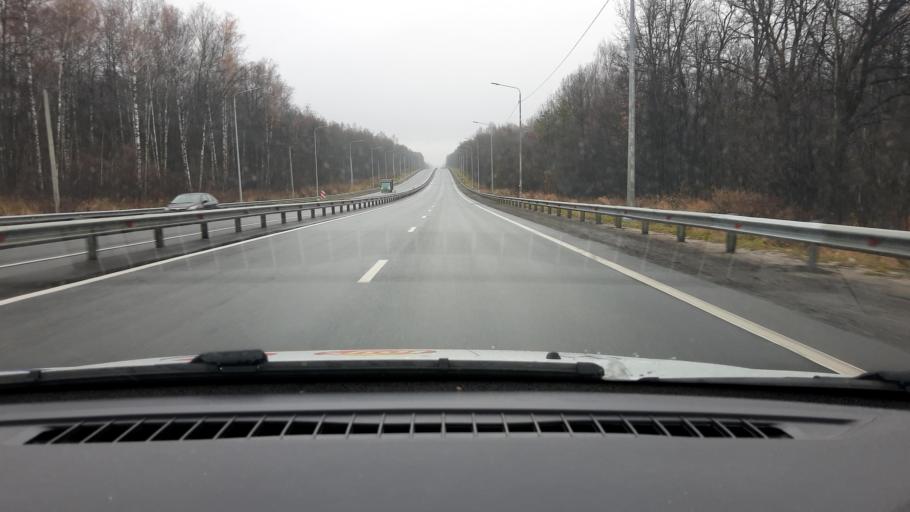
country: RU
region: Nizjnij Novgorod
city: Burevestnik
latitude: 56.0284
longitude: 43.9616
